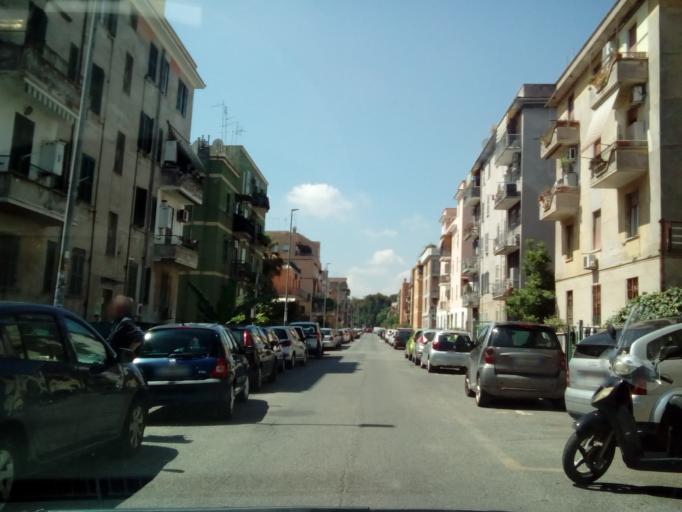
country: IT
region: Latium
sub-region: Citta metropolitana di Roma Capitale
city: Rome
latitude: 41.8773
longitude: 12.5710
